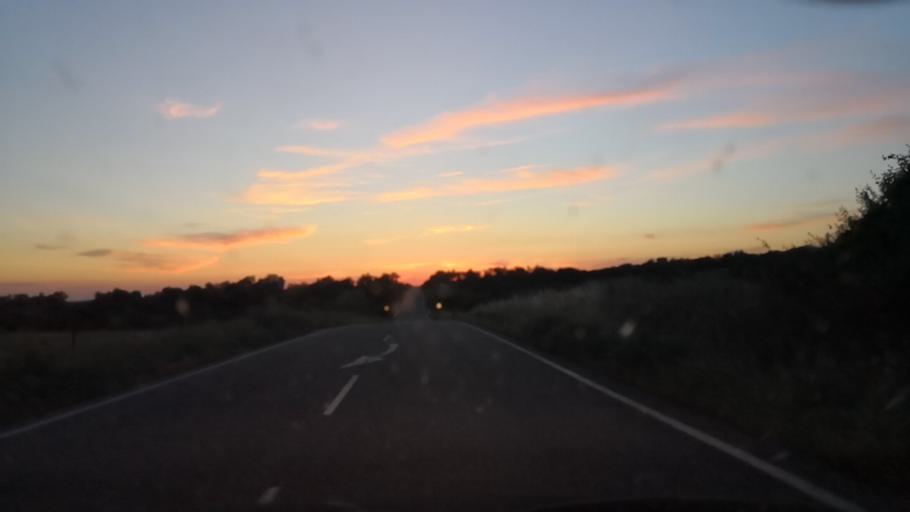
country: ES
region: Extremadura
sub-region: Provincia de Caceres
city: Piedras Albas
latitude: 39.7822
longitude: -6.9330
